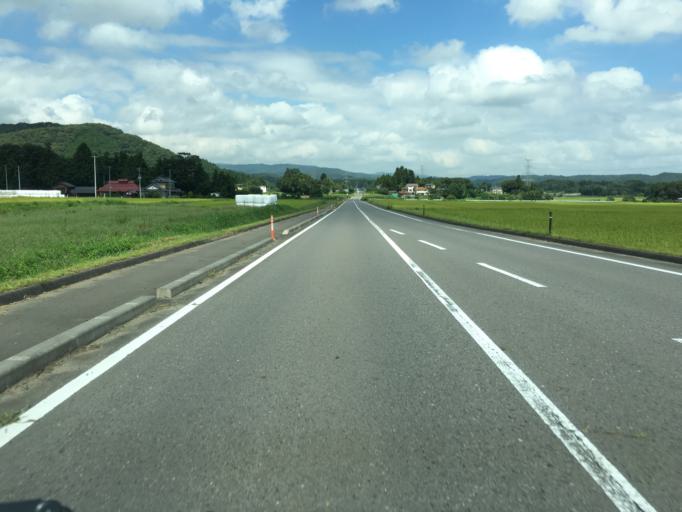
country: JP
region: Fukushima
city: Motomiya
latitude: 37.5564
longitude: 140.3840
